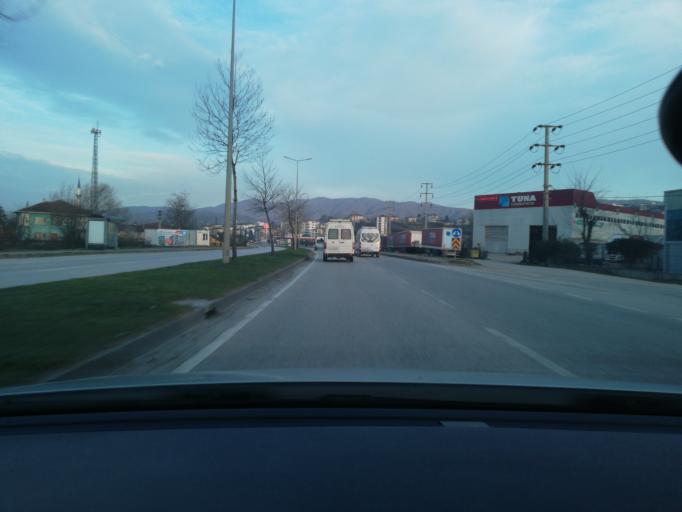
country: TR
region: Duzce
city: Konuralp
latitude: 40.8981
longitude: 31.1634
